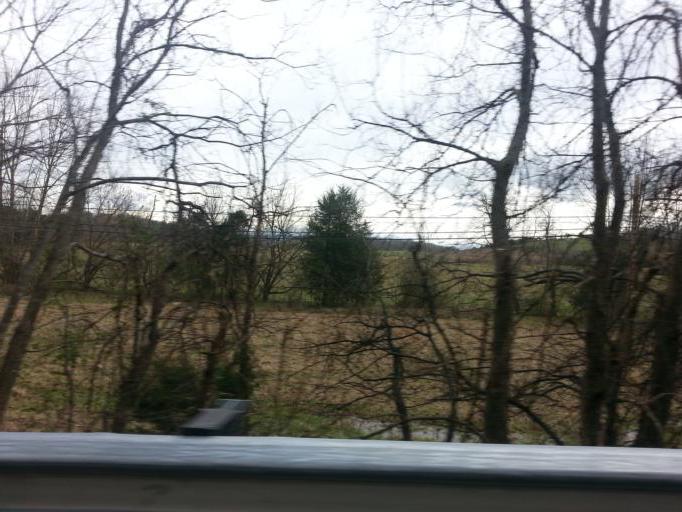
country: US
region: Tennessee
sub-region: Greene County
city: Mosheim
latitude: 36.0816
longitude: -82.9587
